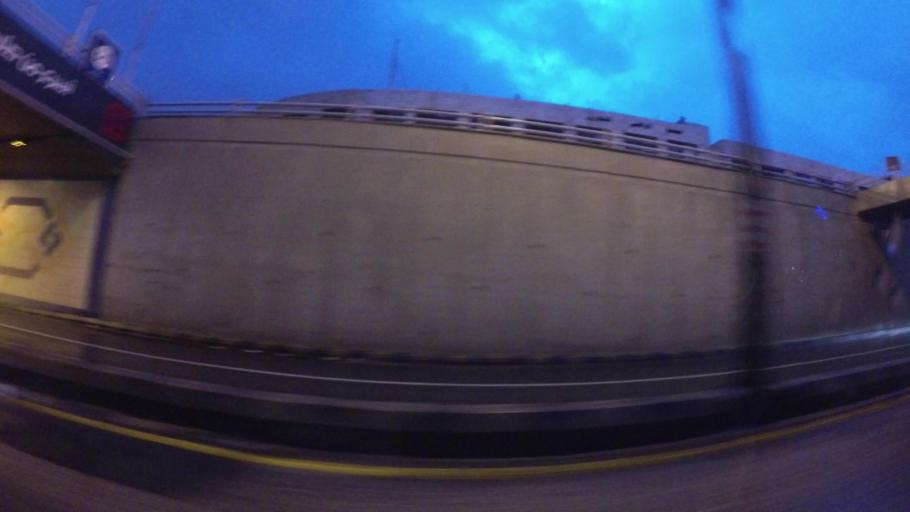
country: JO
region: Amman
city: Al Jubayhah
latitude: 31.9903
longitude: 35.8679
